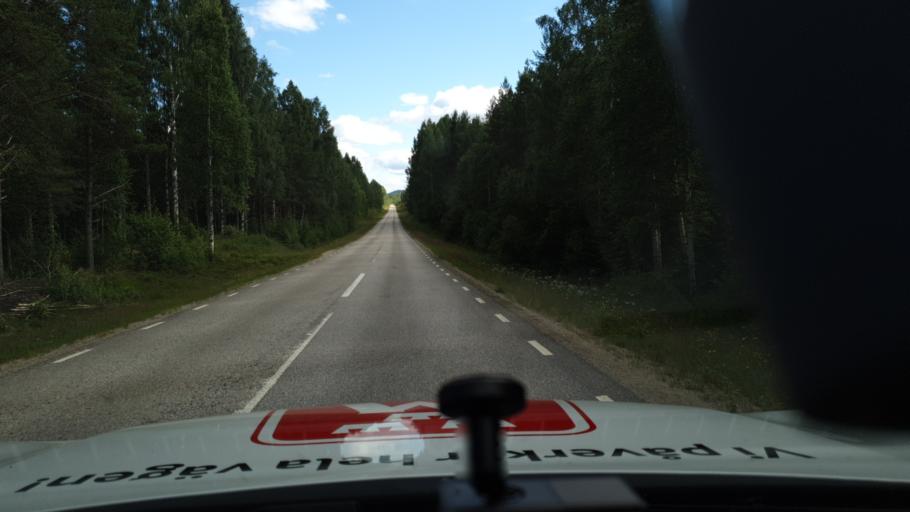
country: NO
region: Hedmark
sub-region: Trysil
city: Innbygda
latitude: 61.0211
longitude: 12.4694
